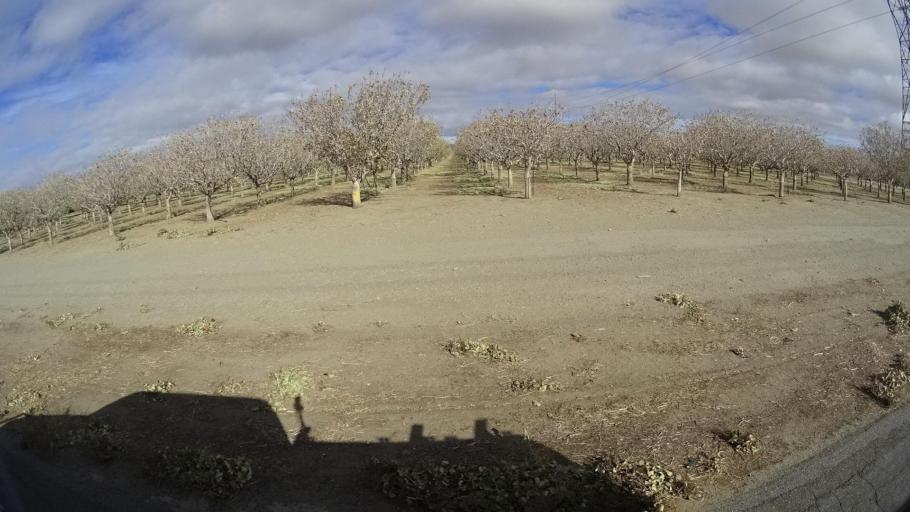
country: US
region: California
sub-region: Kern County
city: Rosamond
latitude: 34.8346
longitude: -118.3200
